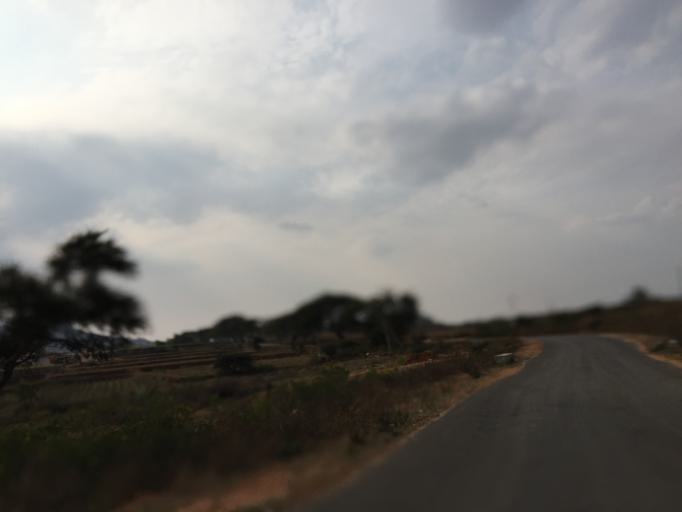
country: IN
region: Karnataka
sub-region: Chikkaballapur
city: Chik Ballapur
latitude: 13.5509
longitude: 77.7587
